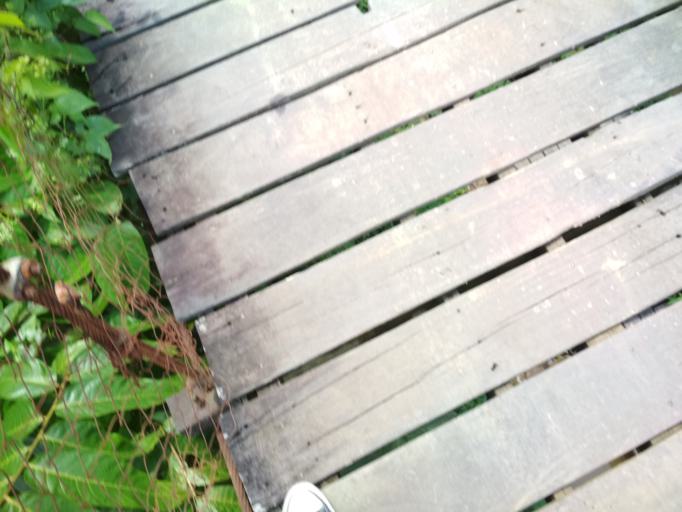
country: ID
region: West Kalimantan
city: Bengkayang
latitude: 0.7525
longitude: 110.1010
